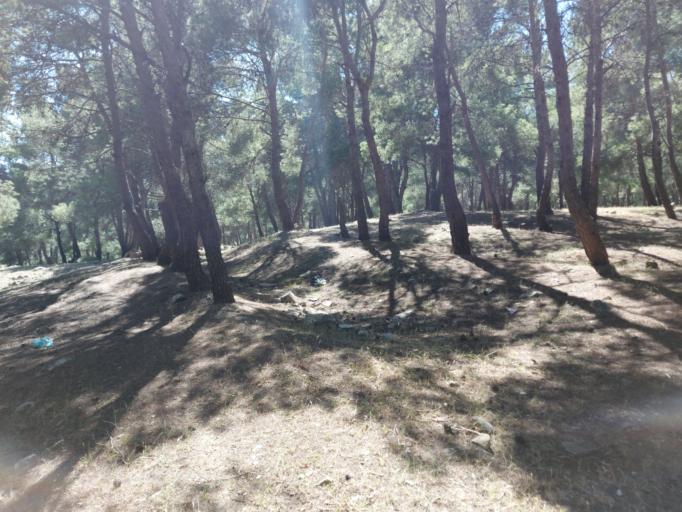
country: TN
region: Kef
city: El Kef
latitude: 36.1851
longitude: 8.7278
